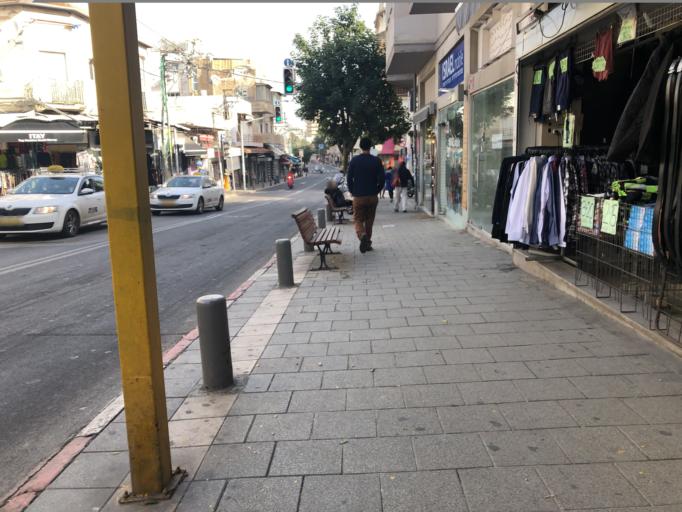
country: IL
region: Tel Aviv
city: Tel Aviv
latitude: 32.0701
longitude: 34.7710
